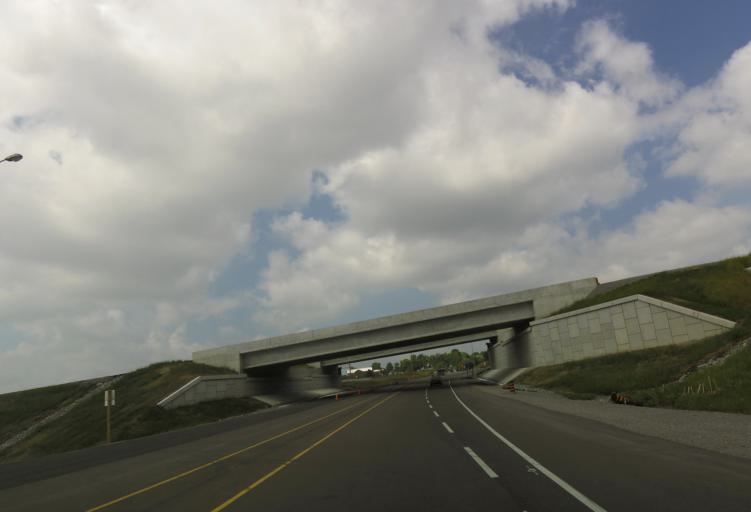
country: CA
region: Ontario
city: Oshawa
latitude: 43.9813
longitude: -78.8682
